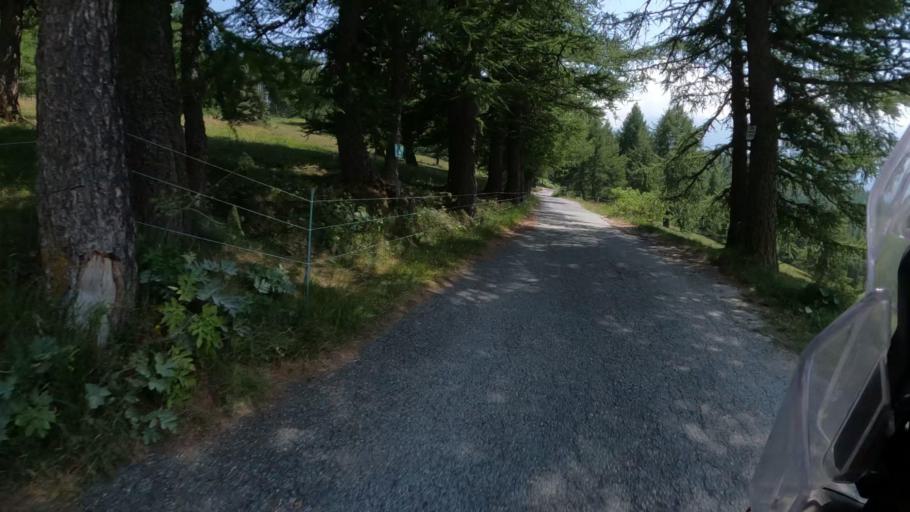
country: IT
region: Piedmont
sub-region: Provincia di Torino
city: Fenestrelle
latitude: 45.0436
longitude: 7.0786
